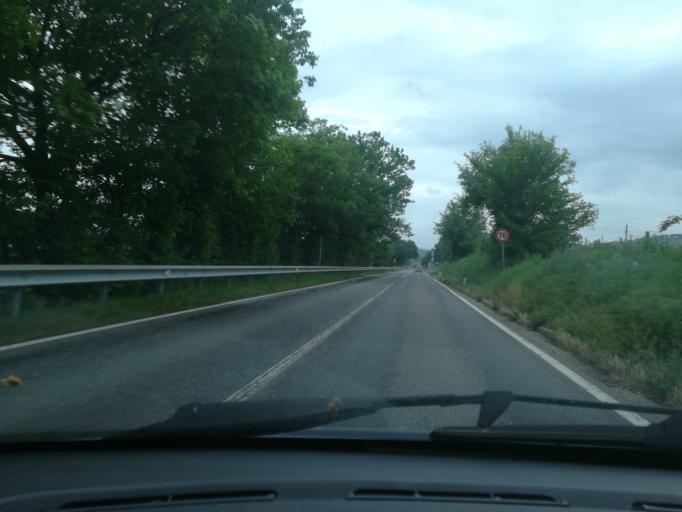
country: IT
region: The Marches
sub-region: Provincia di Macerata
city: Treia
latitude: 43.2690
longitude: 13.2674
